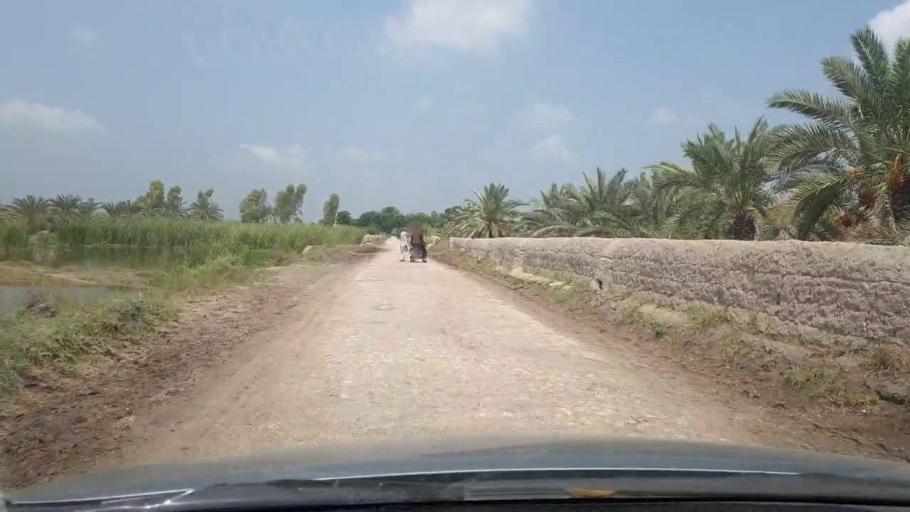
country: PK
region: Sindh
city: Khairpur
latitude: 27.4798
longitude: 68.7126
